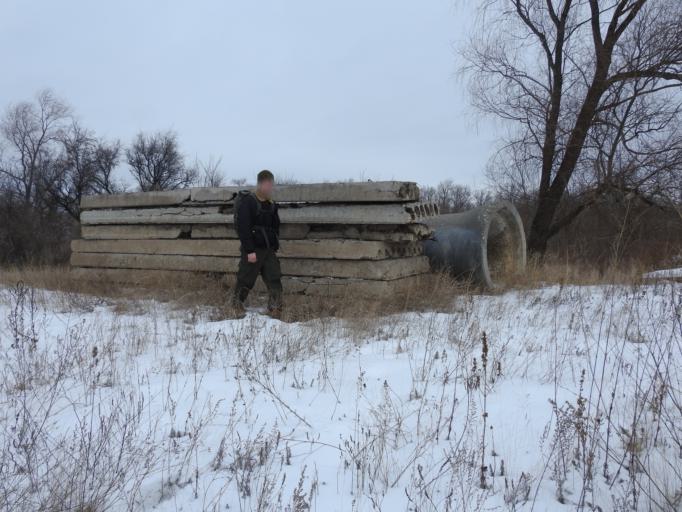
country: RU
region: Saratov
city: Krasnyy Yar
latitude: 51.5461
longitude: 46.5215
